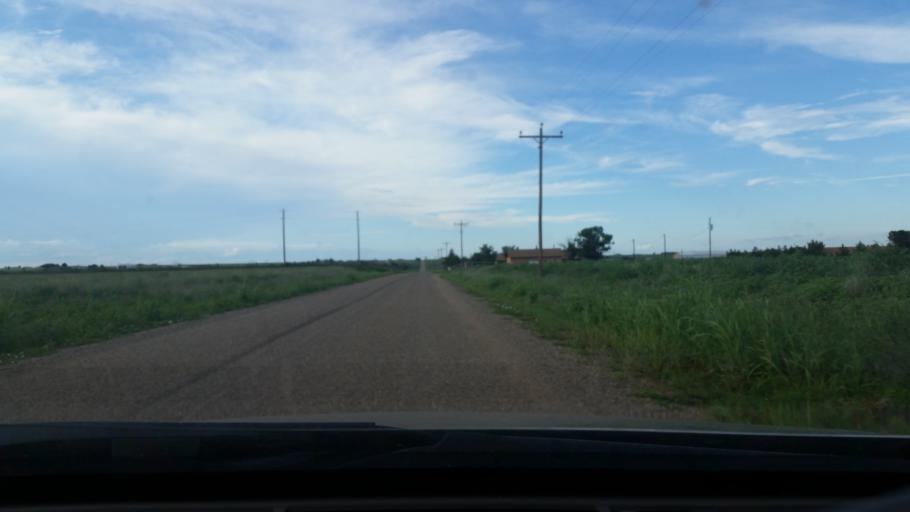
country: US
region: New Mexico
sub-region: Curry County
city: Clovis
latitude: 34.4690
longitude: -103.1789
